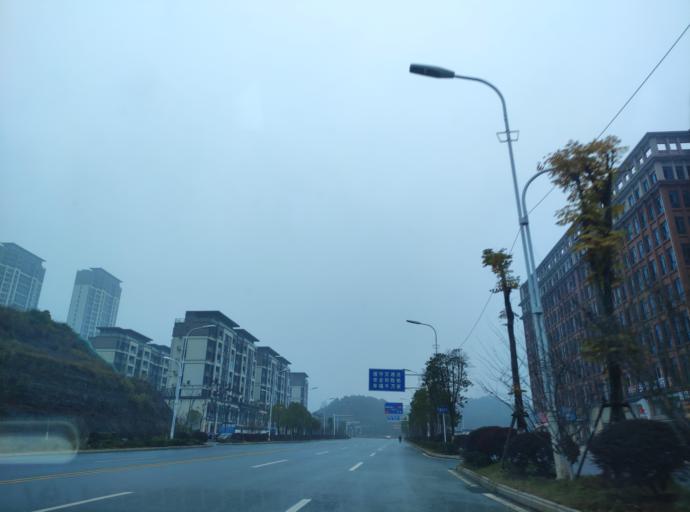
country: CN
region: Jiangxi Sheng
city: Pingxiang
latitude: 27.6681
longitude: 113.8467
